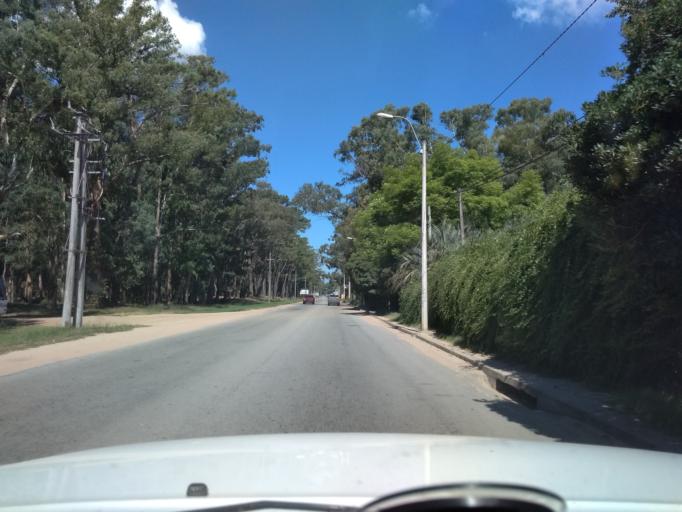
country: UY
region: Canelones
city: Barra de Carrasco
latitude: -34.8623
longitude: -56.0260
